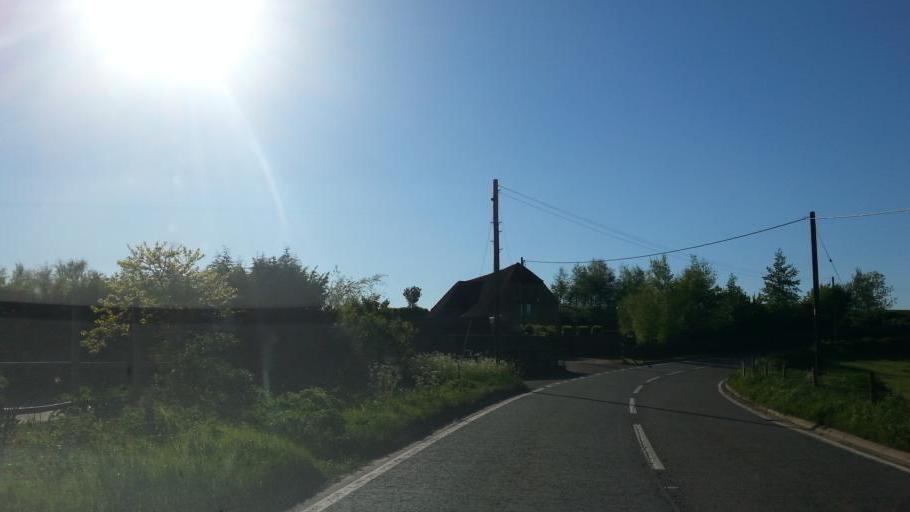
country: GB
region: England
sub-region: Somerset
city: Castle Cary
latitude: 51.0803
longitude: -2.5044
